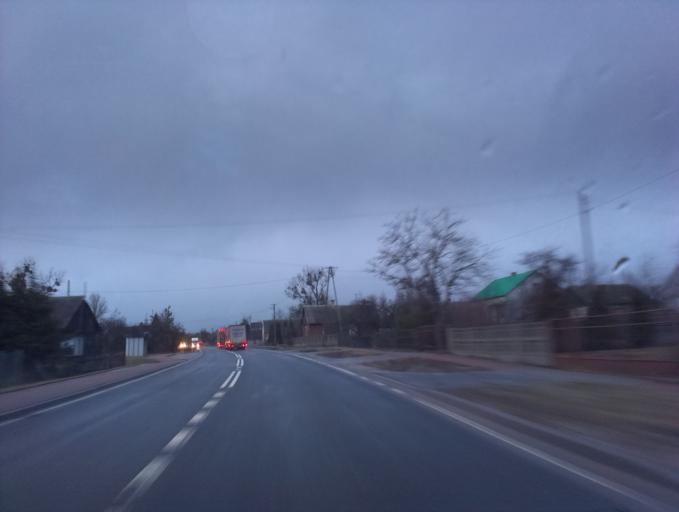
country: PL
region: Lodz Voivodeship
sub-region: Powiat opoczynski
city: Zarnow
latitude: 51.2124
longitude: 20.1955
